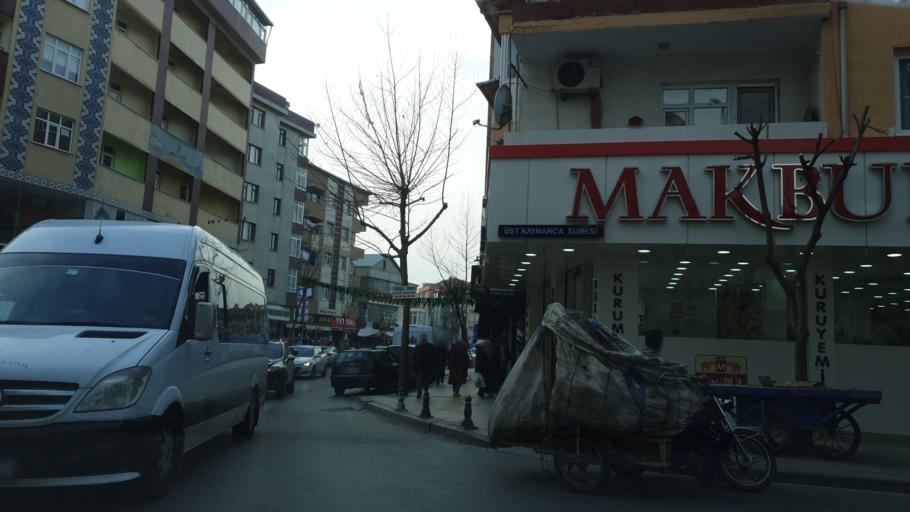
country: TR
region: Istanbul
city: Pendik
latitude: 40.8784
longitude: 29.2676
